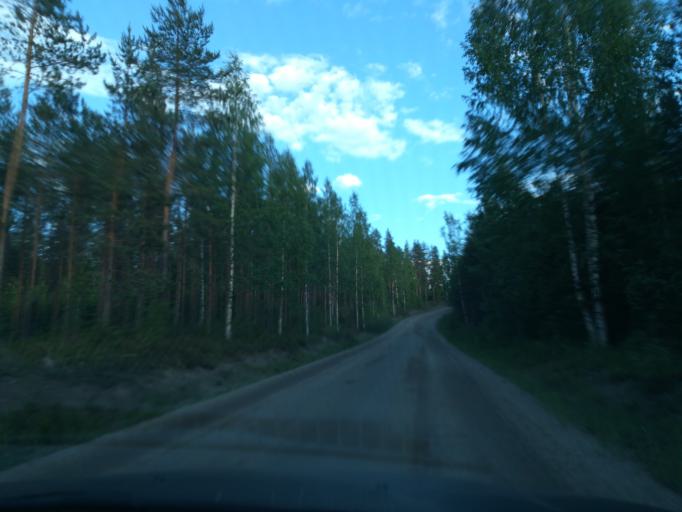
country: FI
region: Southern Savonia
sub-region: Mikkeli
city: Puumala
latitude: 61.6223
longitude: 28.1110
